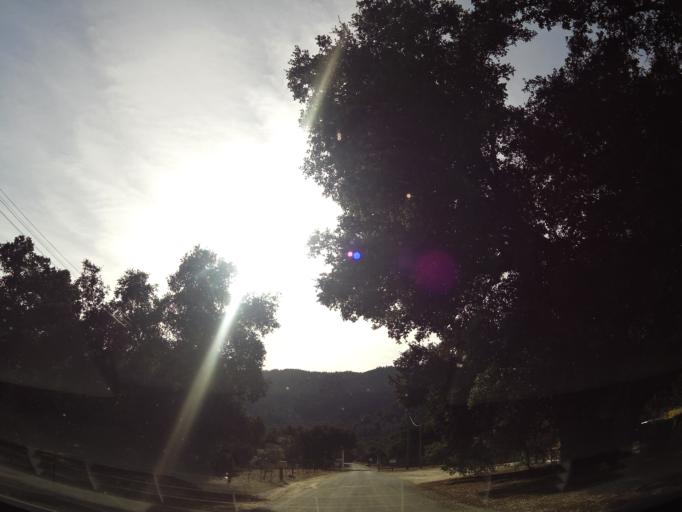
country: US
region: California
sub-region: San Benito County
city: Ridgemark
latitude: 36.6916
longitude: -121.3412
